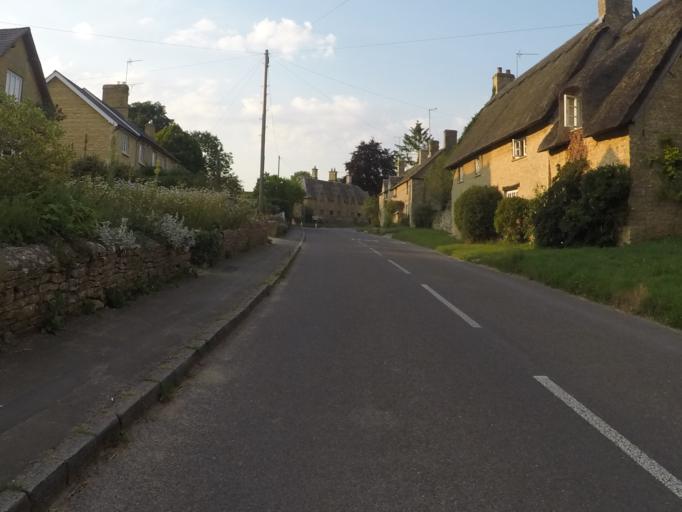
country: GB
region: England
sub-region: Oxfordshire
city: Charlbury
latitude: 51.8927
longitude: -1.4929
